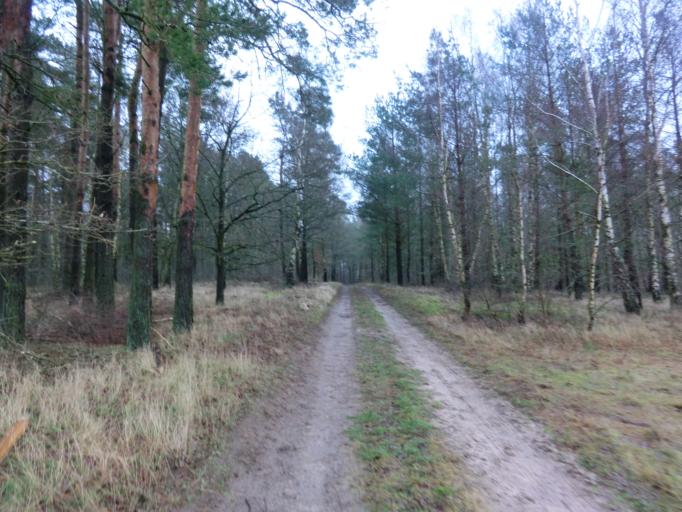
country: SE
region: Skane
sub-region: Hoors Kommun
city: Loberod
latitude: 55.7300
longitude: 13.3970
